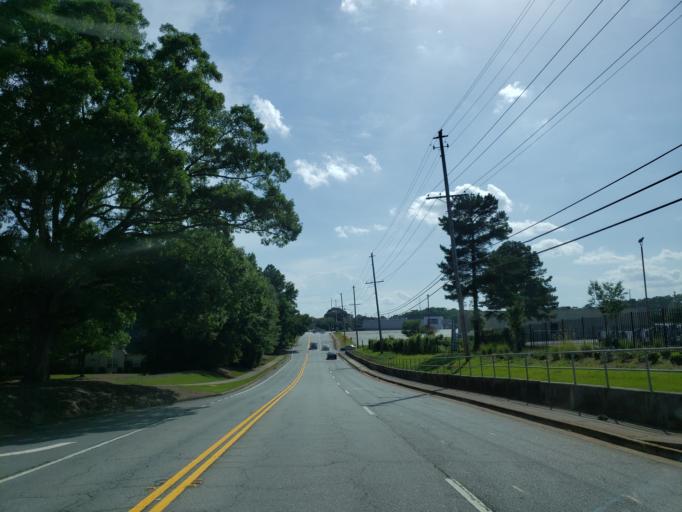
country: US
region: Georgia
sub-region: Cobb County
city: Mableton
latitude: 33.8630
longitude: -84.5916
